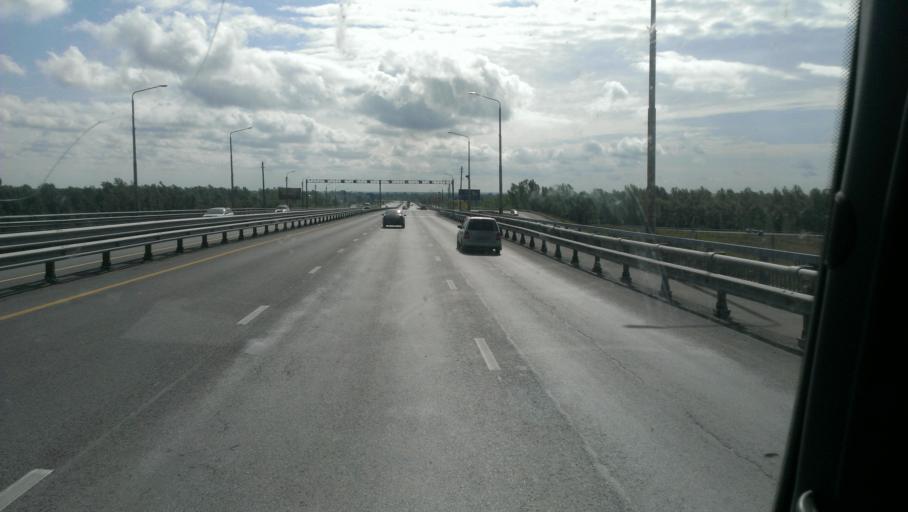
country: RU
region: Altai Krai
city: Zaton
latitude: 53.3214
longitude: 83.8093
